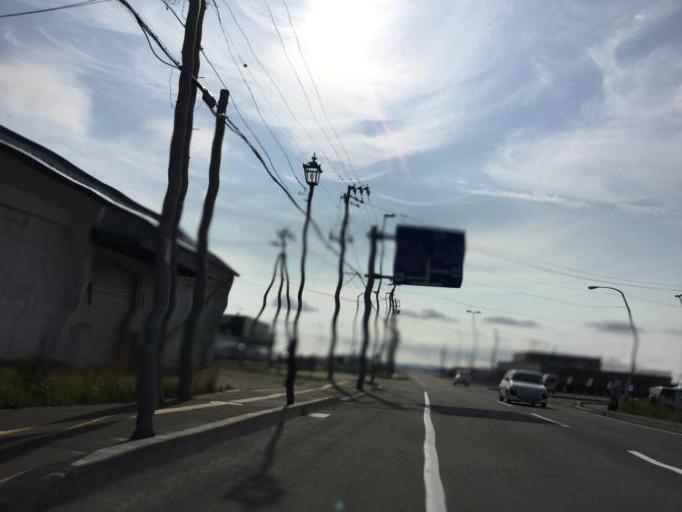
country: JP
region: Hokkaido
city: Wakkanai
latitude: 45.4152
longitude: 141.6810
